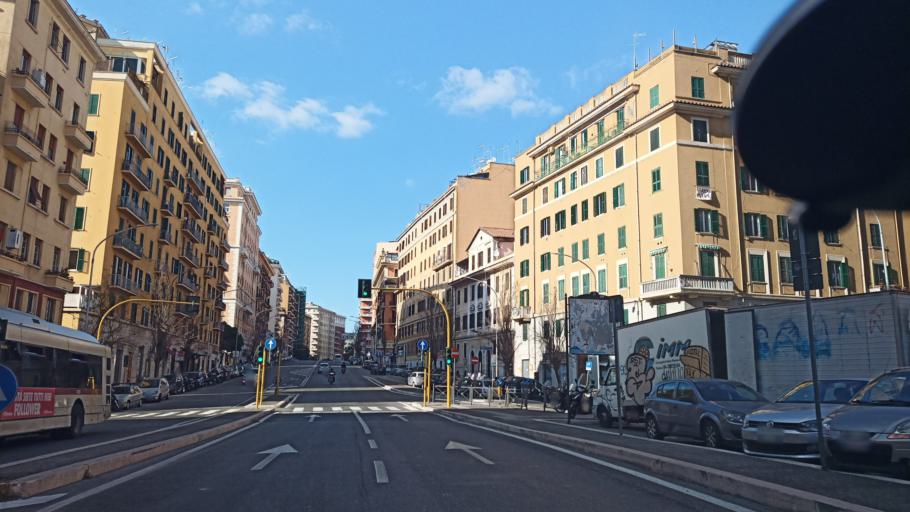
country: IT
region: Latium
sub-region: Citta metropolitana di Roma Capitale
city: Rome
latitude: 41.8781
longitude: 12.5084
